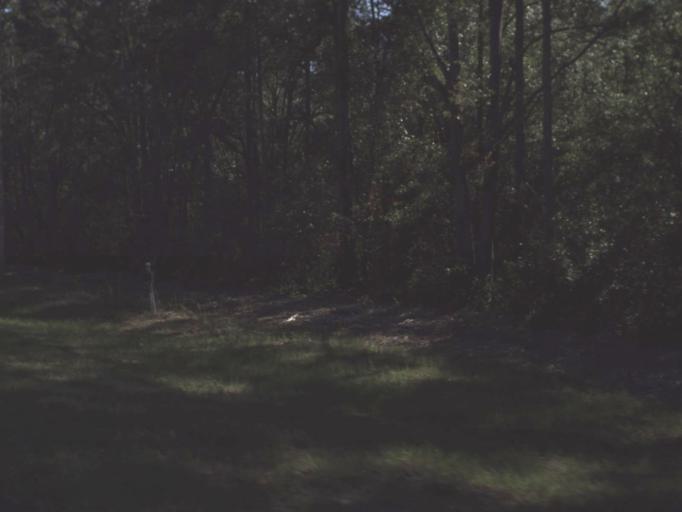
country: US
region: Florida
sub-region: Marion County
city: Dunnellon
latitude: 29.1169
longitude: -82.4476
